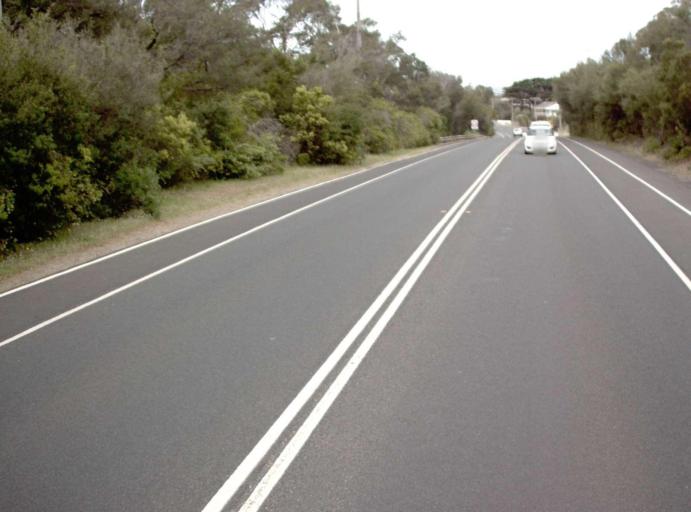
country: AU
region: Victoria
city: Rye
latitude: -38.3678
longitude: 144.8100
